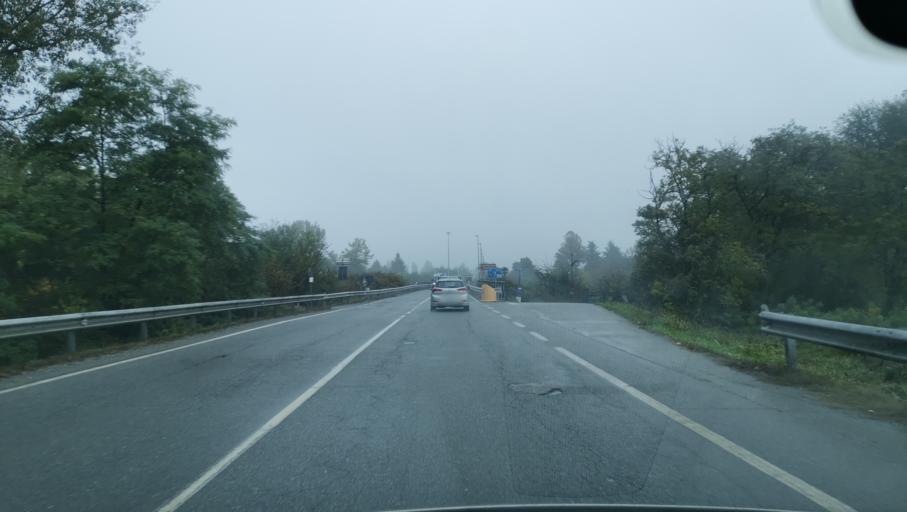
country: IT
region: Piedmont
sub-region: Provincia di Torino
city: Castiglione Torinese
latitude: 45.1288
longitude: 7.7849
